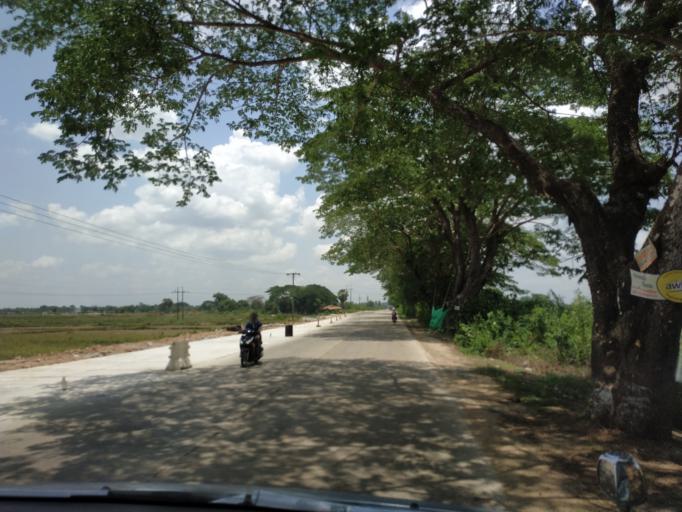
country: MM
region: Bago
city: Bago
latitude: 17.4786
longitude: 96.4958
